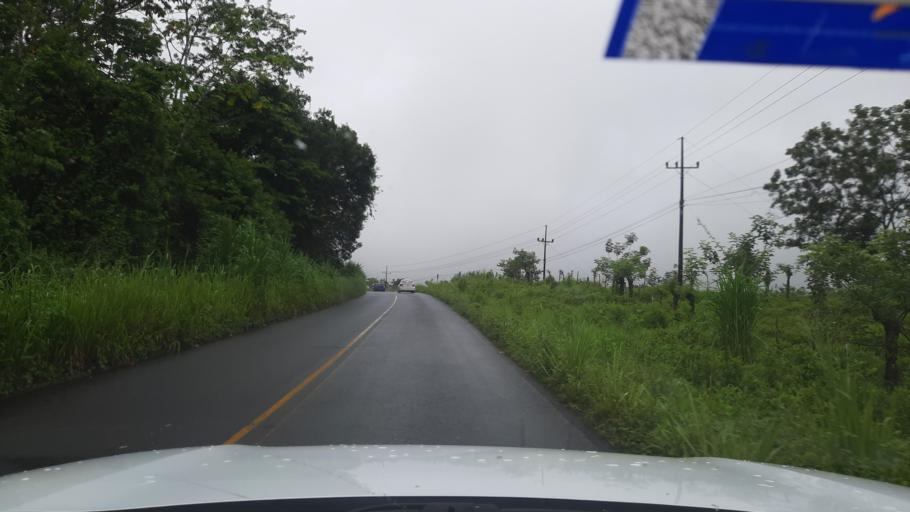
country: CR
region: Alajuela
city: Bijagua
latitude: 10.7765
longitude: -85.0287
